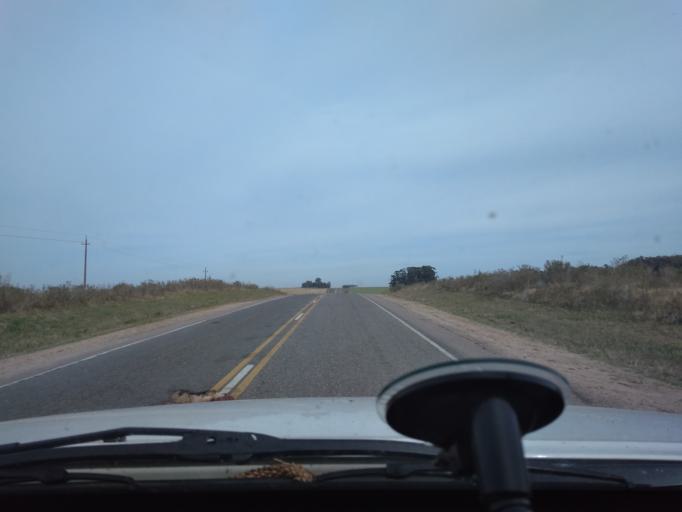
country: UY
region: Florida
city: Florida
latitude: -34.0417
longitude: -55.9632
